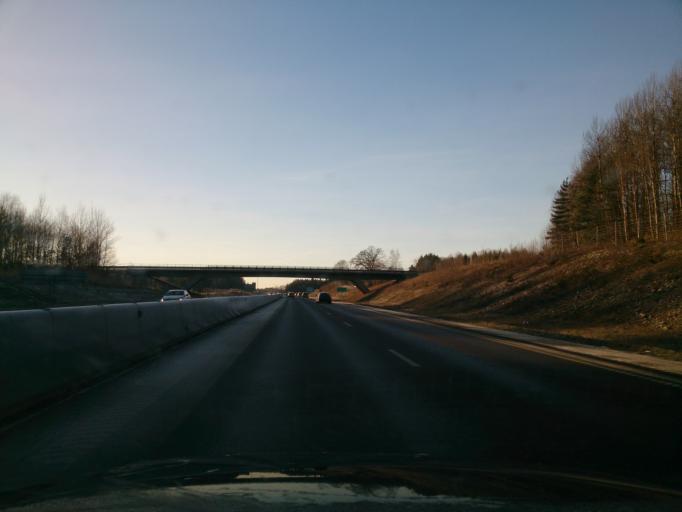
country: SE
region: OEstergoetland
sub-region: Norrkopings Kommun
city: Norrkoping
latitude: 58.5749
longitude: 16.0952
